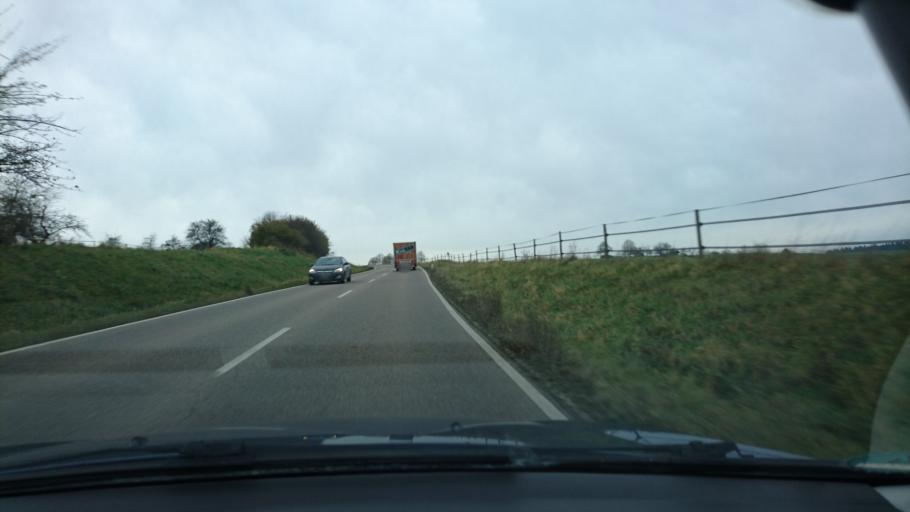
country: DE
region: Baden-Wuerttemberg
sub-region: Regierungsbezirk Stuttgart
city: Welzheim
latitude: 48.8846
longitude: 9.6404
